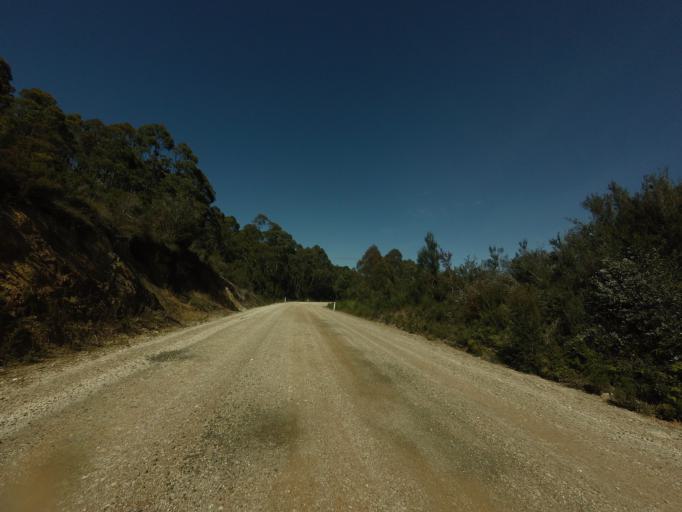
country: AU
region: Tasmania
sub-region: Huon Valley
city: Geeveston
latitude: -42.9947
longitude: 146.3707
